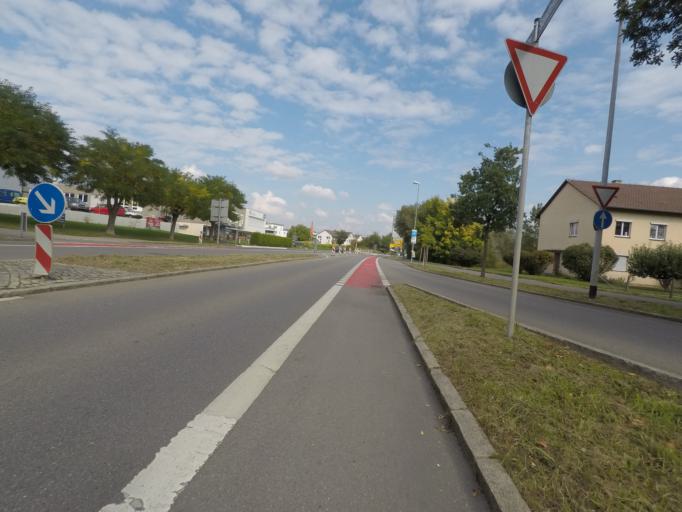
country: DE
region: Baden-Wuerttemberg
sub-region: Tuebingen Region
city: Reutlingen
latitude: 48.5119
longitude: 9.2200
